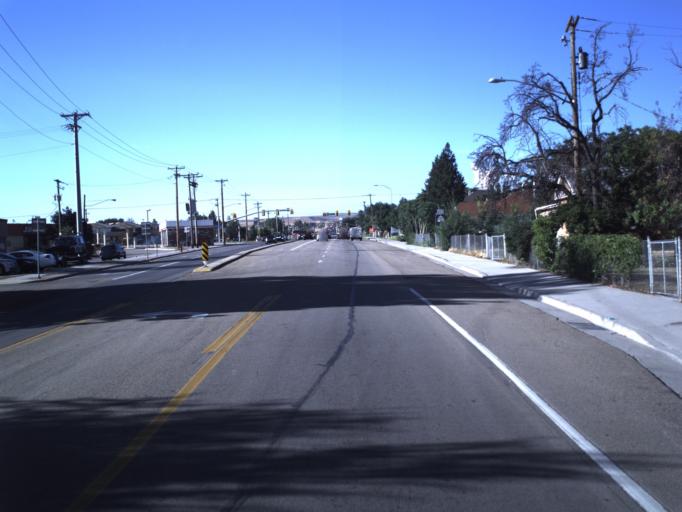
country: US
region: Utah
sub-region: Salt Lake County
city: Magna
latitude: 40.6985
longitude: -112.0919
